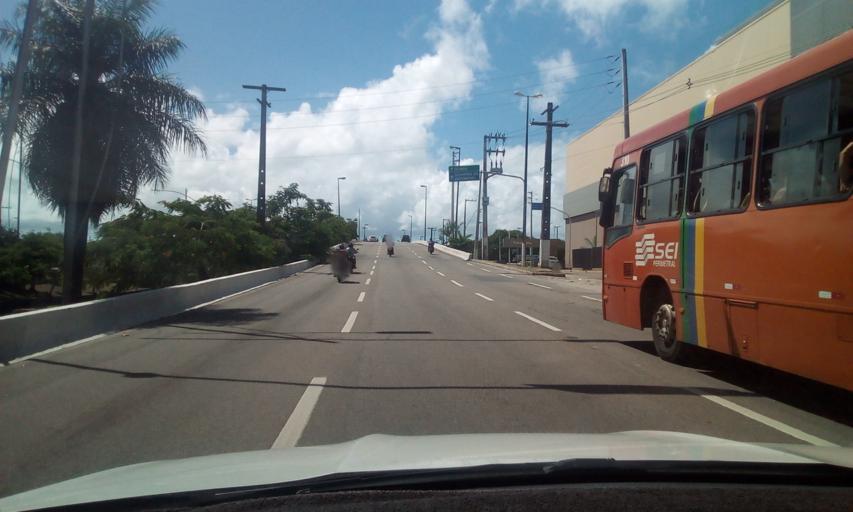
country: BR
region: Pernambuco
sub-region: Recife
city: Recife
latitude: -8.0370
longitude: -34.8726
